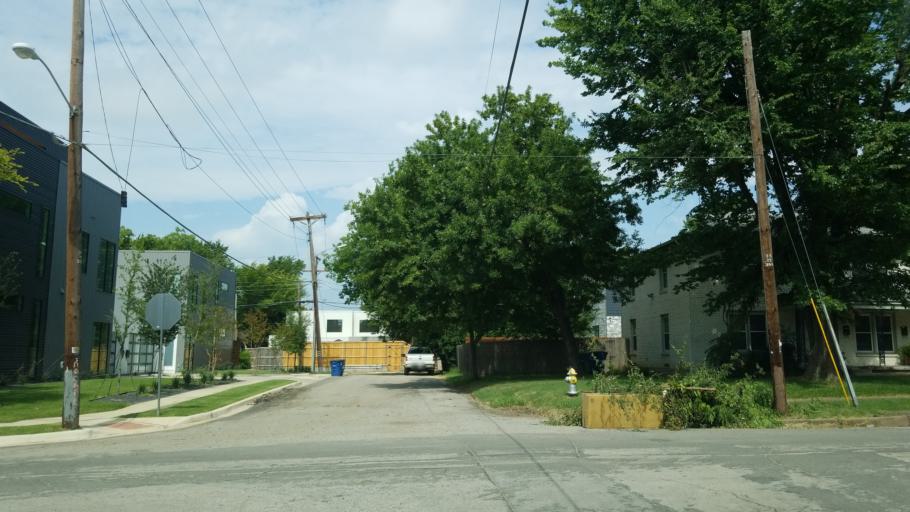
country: US
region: Texas
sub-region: Dallas County
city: Highland Park
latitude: 32.8134
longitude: -96.7734
